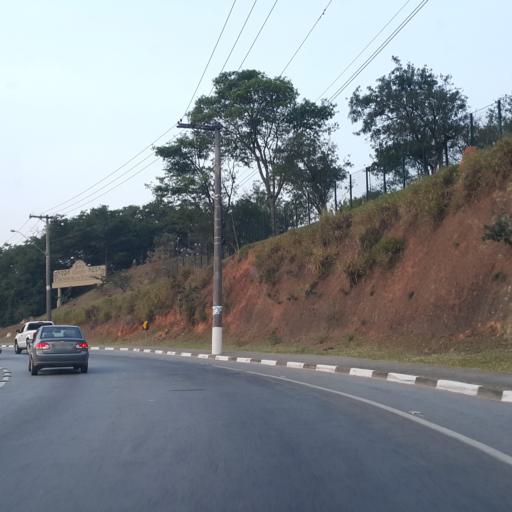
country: BR
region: Sao Paulo
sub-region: Vinhedo
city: Vinhedo
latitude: -23.0480
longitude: -46.9851
